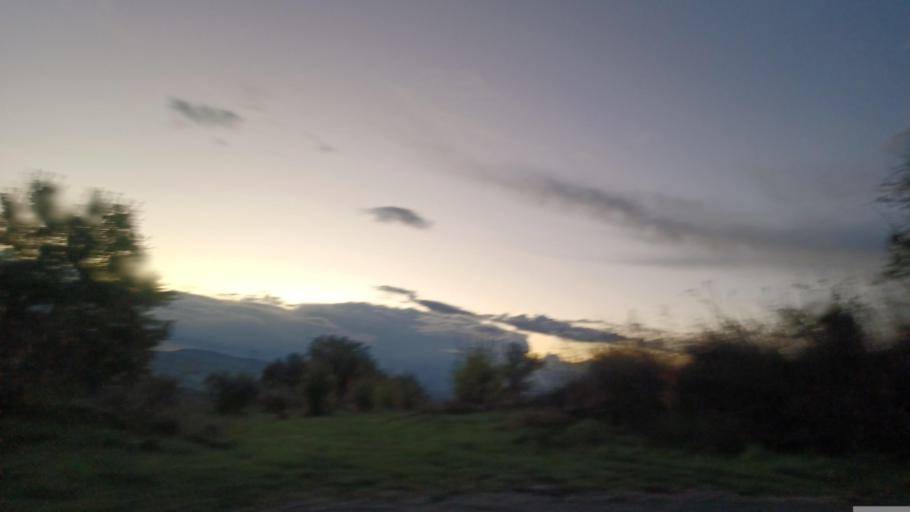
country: CY
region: Pafos
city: Mesogi
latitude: 34.8571
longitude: 32.5030
